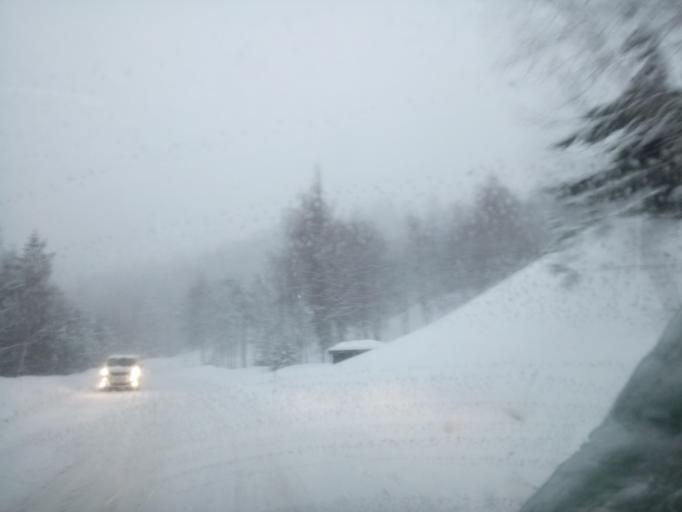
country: FR
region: Rhone-Alpes
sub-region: Departement de la Savoie
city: Modane
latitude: 45.2036
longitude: 6.7003
